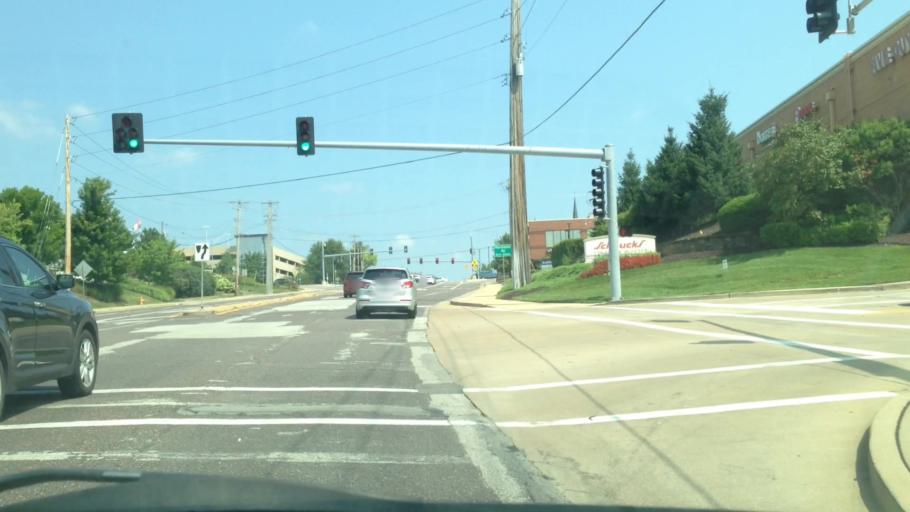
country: US
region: Missouri
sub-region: Saint Louis County
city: Des Peres
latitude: 38.6017
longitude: -90.4439
